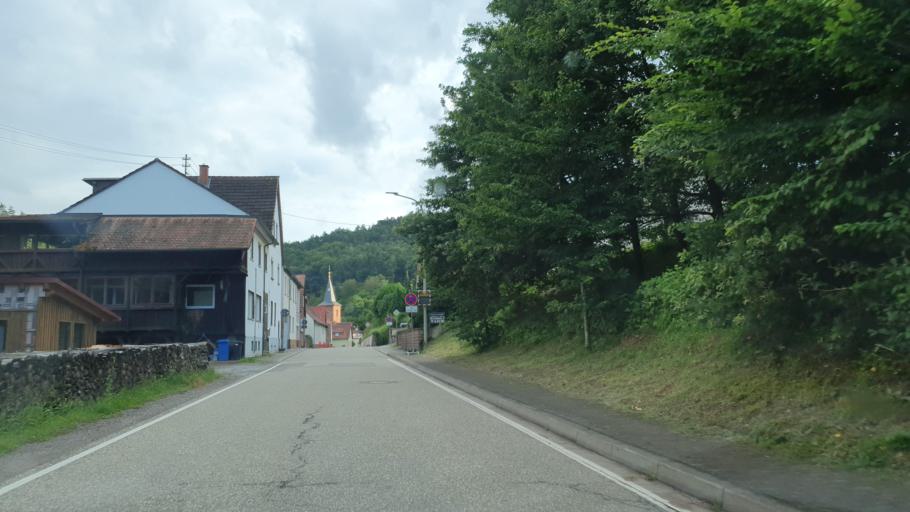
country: DE
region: Rheinland-Pfalz
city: Lug
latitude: 49.1842
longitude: 7.8980
